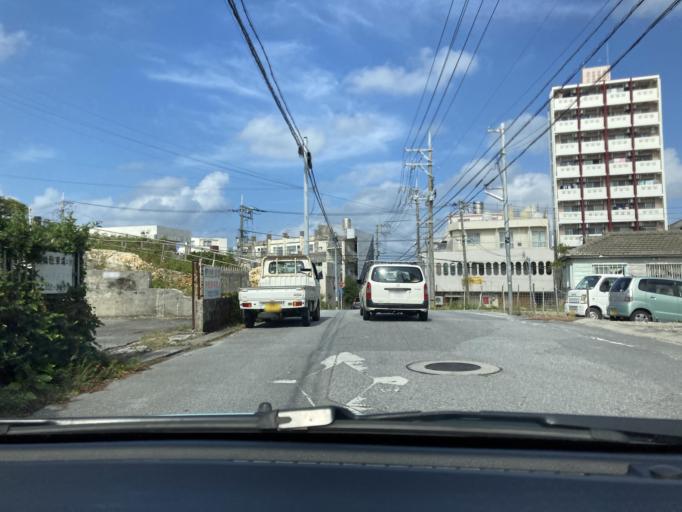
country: JP
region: Okinawa
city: Chatan
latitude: 26.2906
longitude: 127.7770
